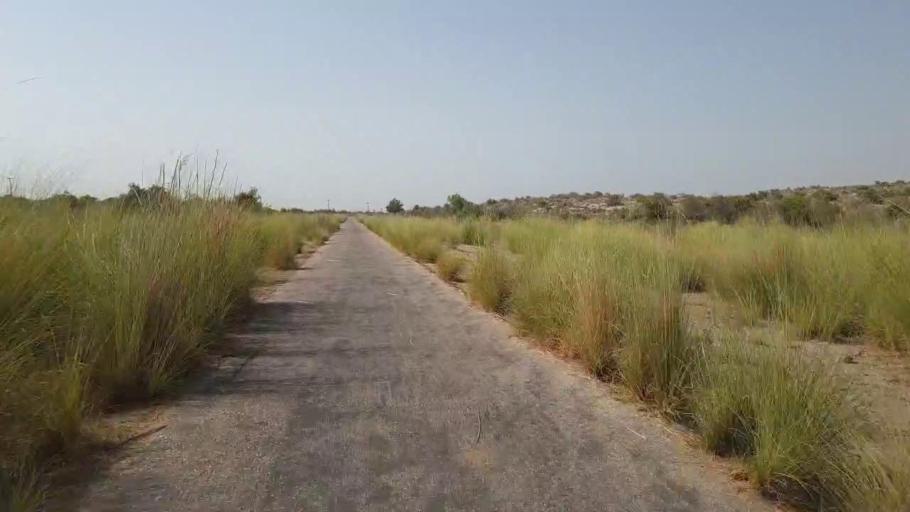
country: PK
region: Sindh
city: Jam Sahib
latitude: 26.5753
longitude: 68.9215
